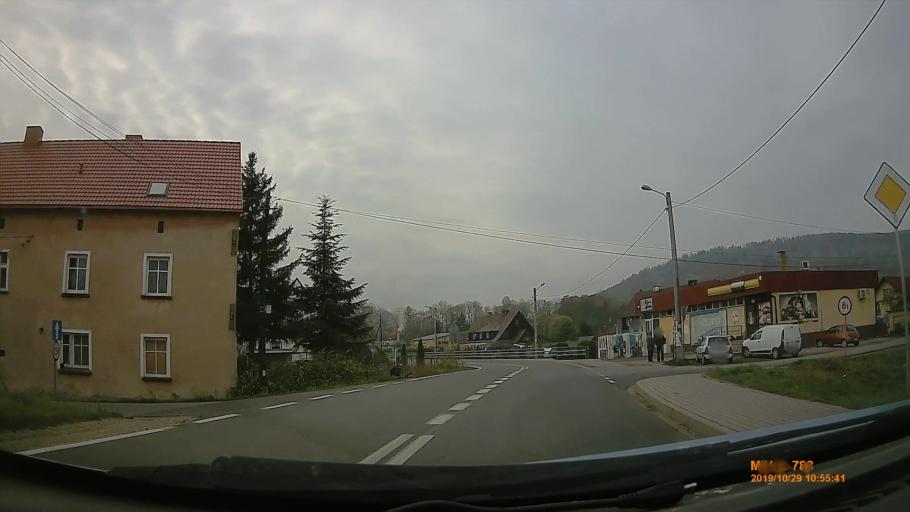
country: PL
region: Lower Silesian Voivodeship
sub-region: Powiat klodzki
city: Nowa Ruda
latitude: 50.5188
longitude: 16.4926
